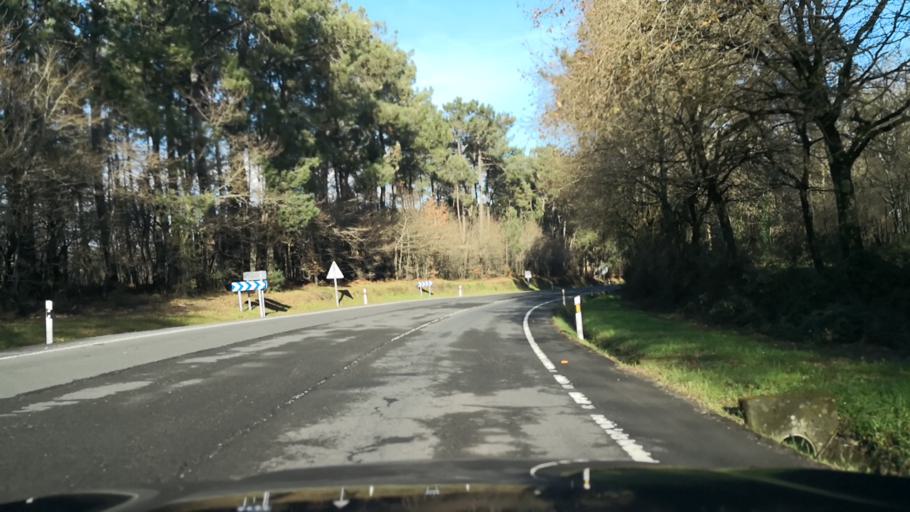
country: ES
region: Galicia
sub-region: Provincia de Pontevedra
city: Silleda
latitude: 42.7045
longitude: -8.3098
